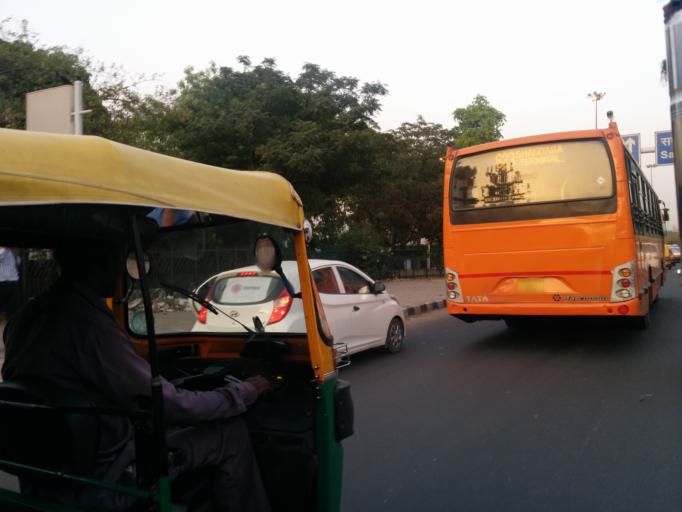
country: IN
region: NCT
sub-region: New Delhi
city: New Delhi
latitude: 28.5697
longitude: 77.2055
